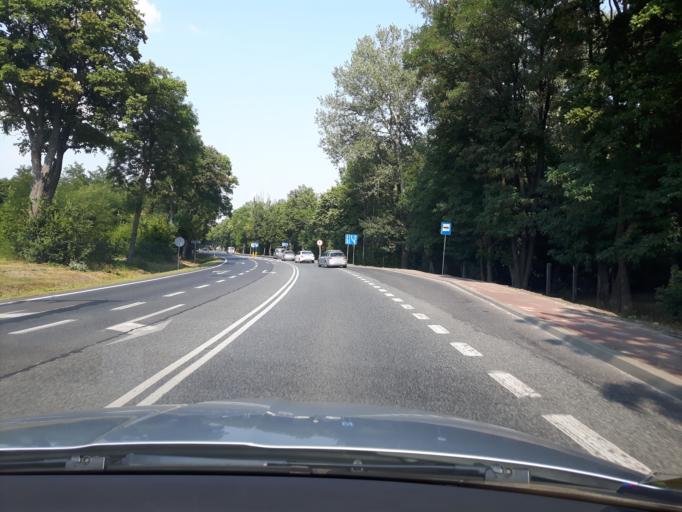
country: PL
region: Masovian Voivodeship
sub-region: Powiat nowodworski
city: Zakroczym
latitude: 52.4426
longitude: 20.6602
